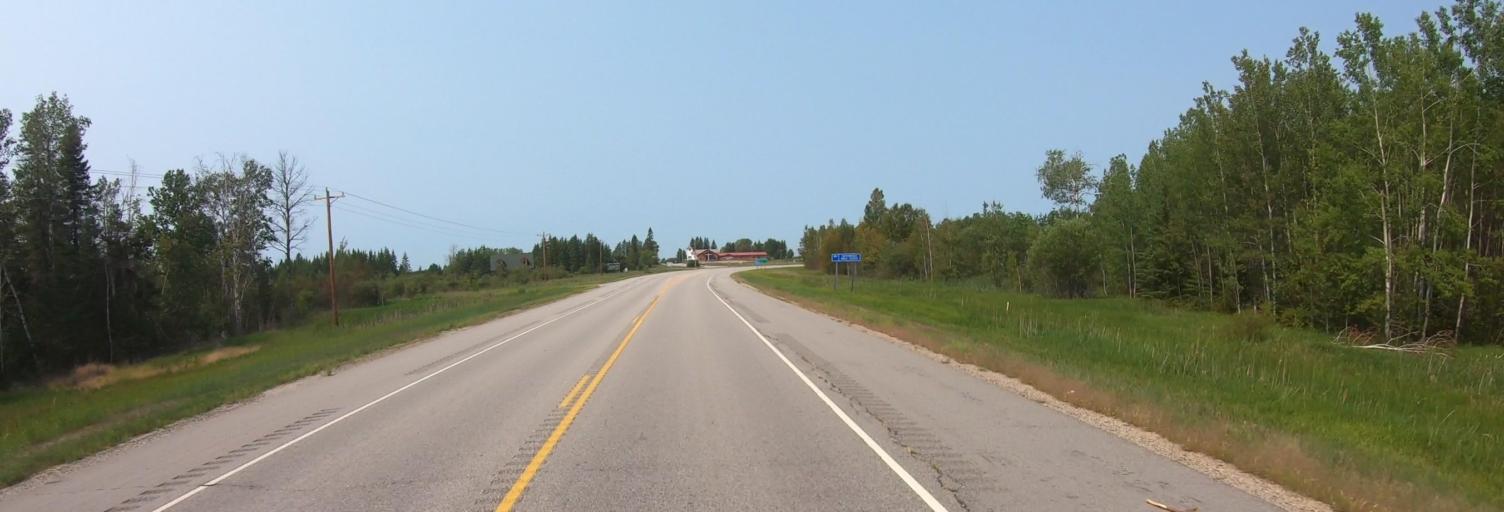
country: CA
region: Ontario
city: Fort Frances
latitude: 48.4108
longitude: -93.1978
